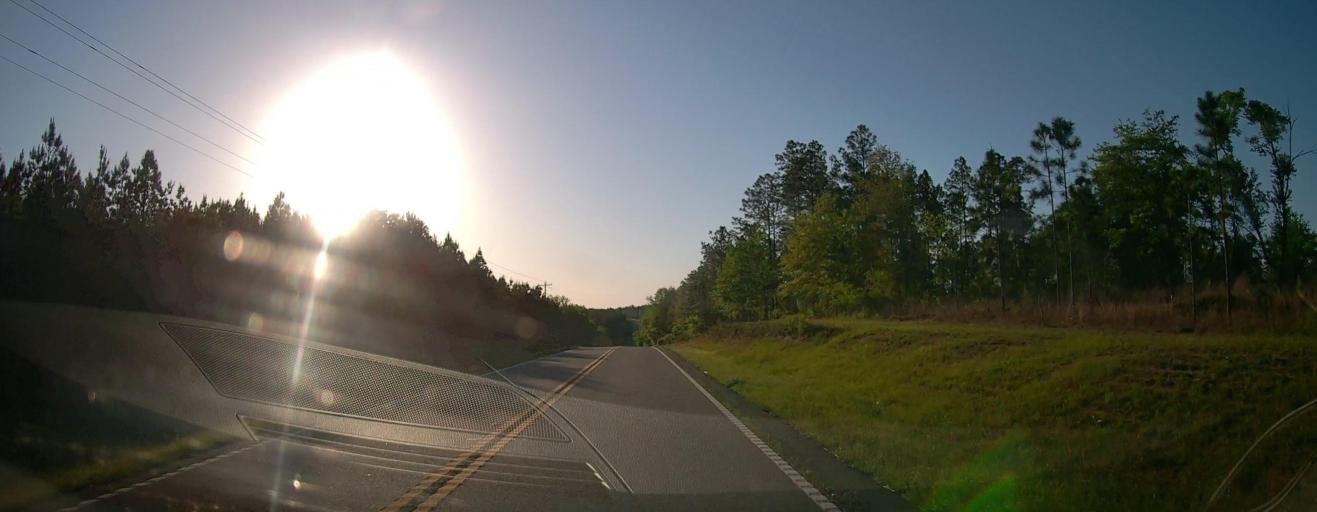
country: US
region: Georgia
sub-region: Schley County
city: Ellaville
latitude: 32.3245
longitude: -84.3229
